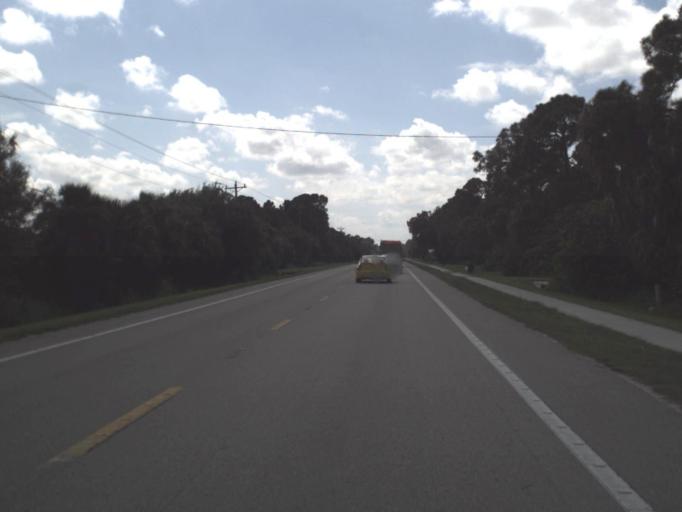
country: US
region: Florida
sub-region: Collier County
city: Immokalee
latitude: 26.5554
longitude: -81.4358
